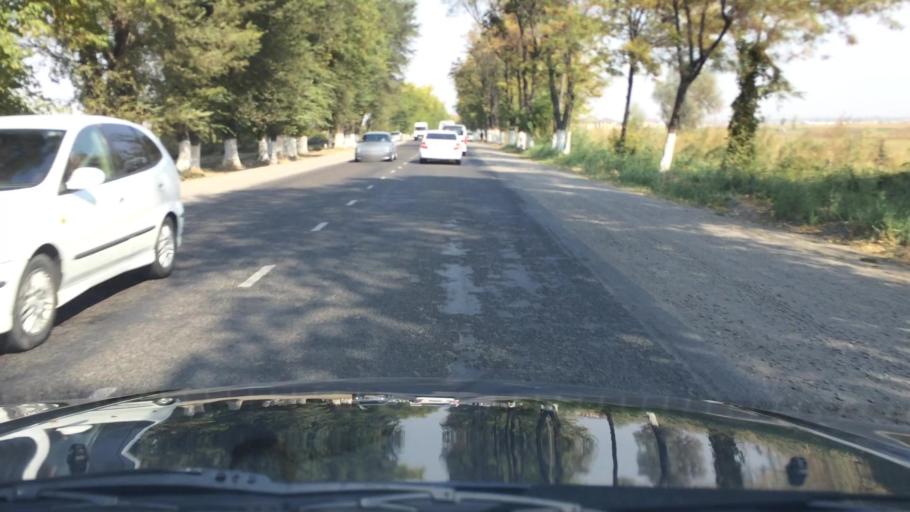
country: KG
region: Chuy
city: Lebedinovka
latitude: 42.9032
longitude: 74.6858
